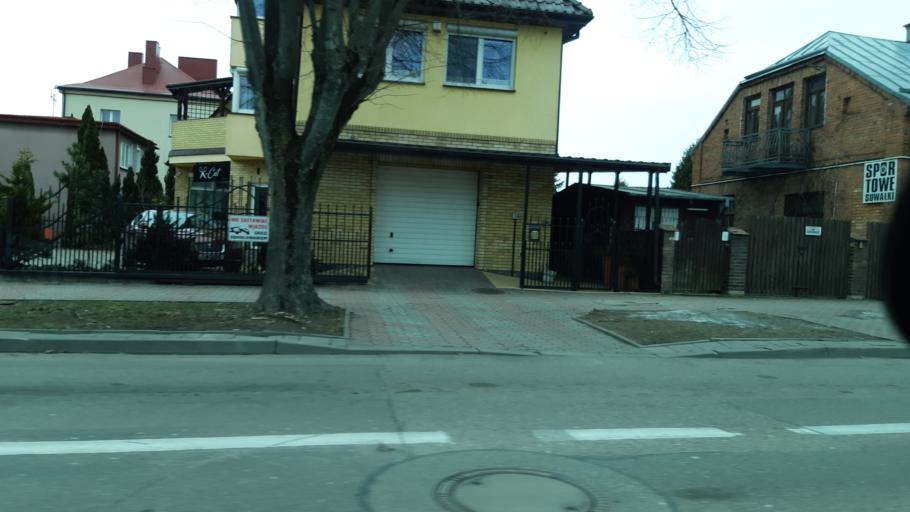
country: PL
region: Podlasie
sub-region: Suwalki
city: Suwalki
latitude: 54.1068
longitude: 22.9316
